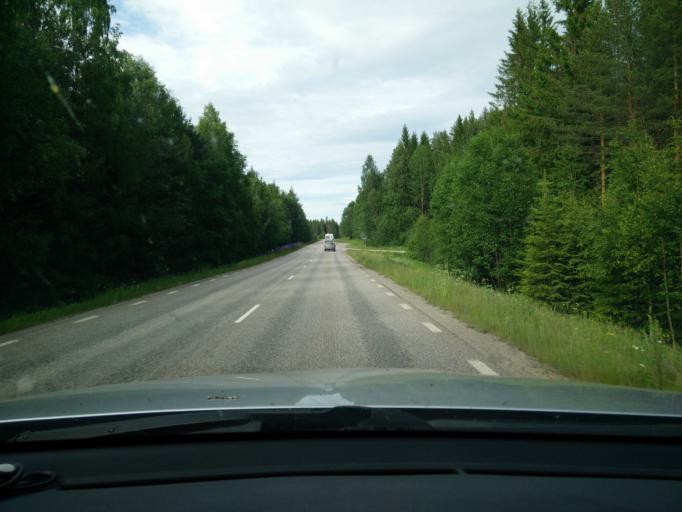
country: SE
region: Gaevleborg
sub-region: Nordanstigs Kommun
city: Bergsjoe
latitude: 61.9318
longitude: 17.0354
